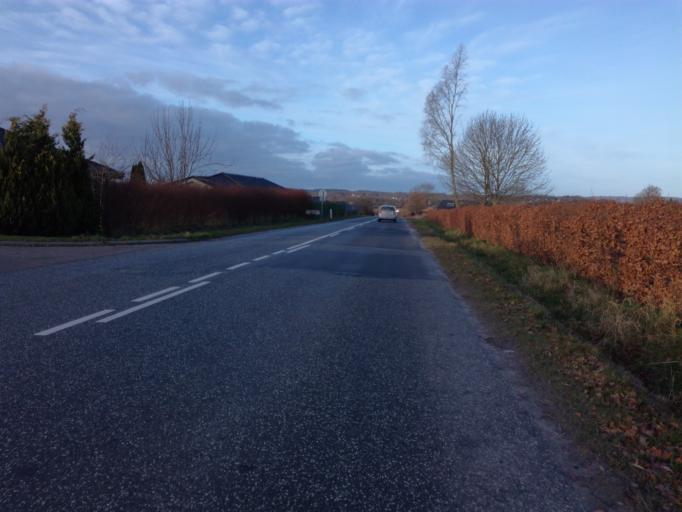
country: DK
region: South Denmark
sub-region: Fredericia Kommune
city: Fredericia
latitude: 55.6164
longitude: 9.7448
